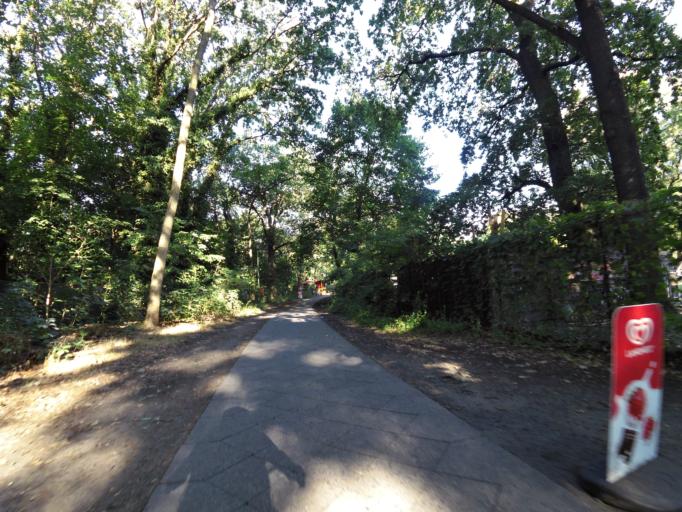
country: DE
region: Berlin
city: Nikolassee
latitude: 52.4329
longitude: 13.1907
